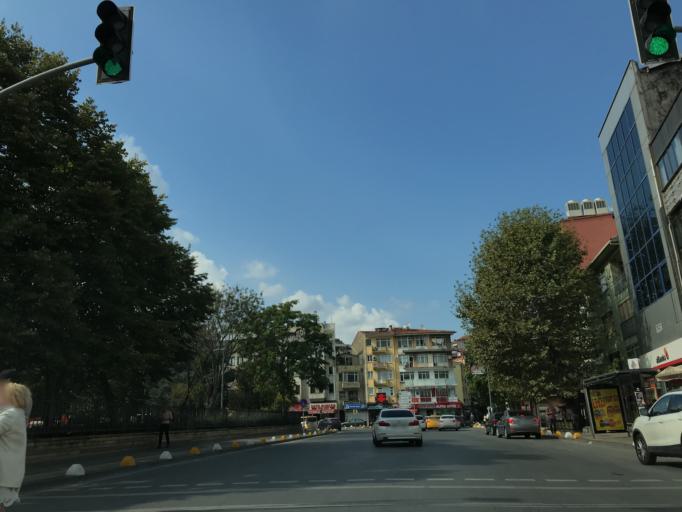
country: TR
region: Istanbul
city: UEskuedar
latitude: 40.9936
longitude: 29.0382
